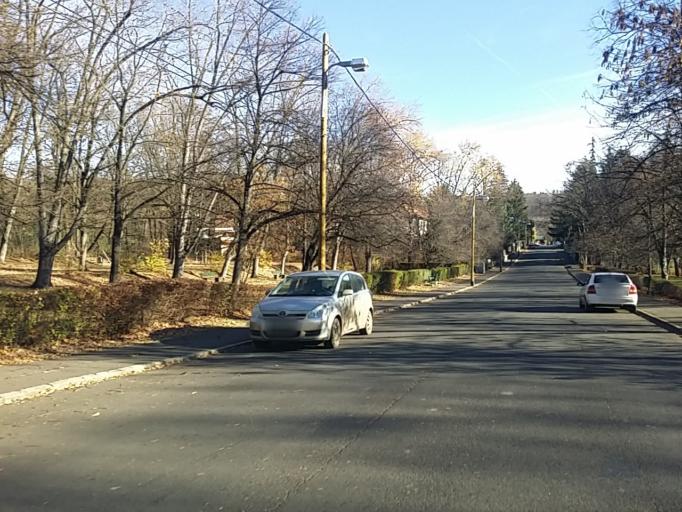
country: HU
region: Heves
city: Gyongyossolymos
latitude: 47.8304
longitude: 19.9649
